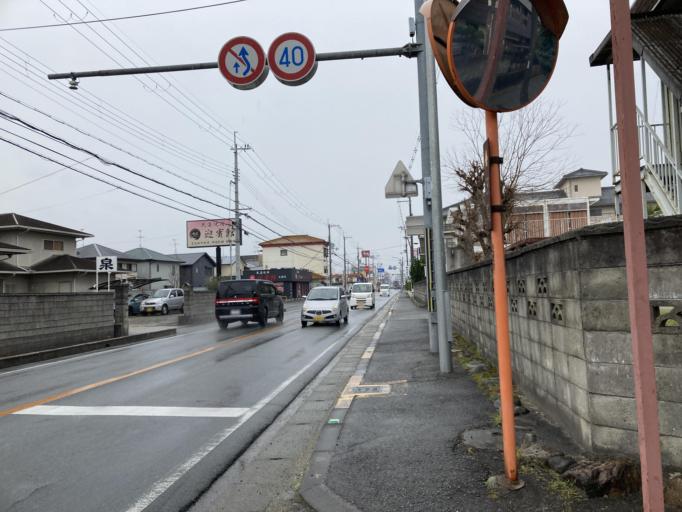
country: JP
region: Nara
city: Tenri
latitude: 34.5911
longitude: 135.8364
